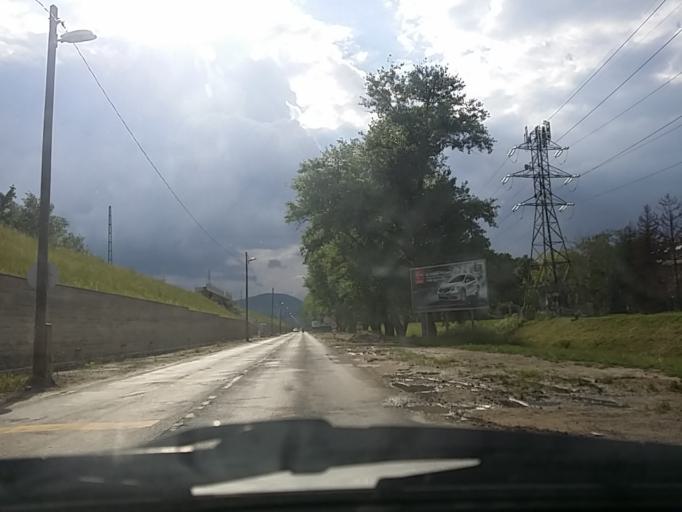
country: HU
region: Budapest
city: Budapest III. keruelet
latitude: 47.5649
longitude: 19.0609
